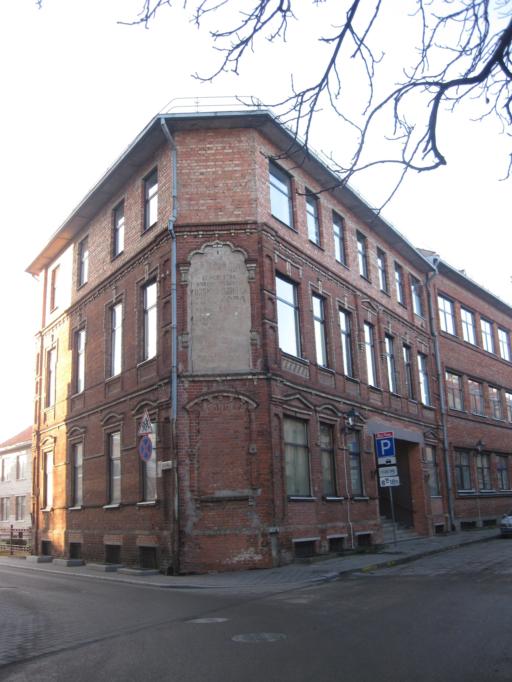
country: LT
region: Kauno apskritis
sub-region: Kaunas
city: Kaunas
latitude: 54.8969
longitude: 23.9005
